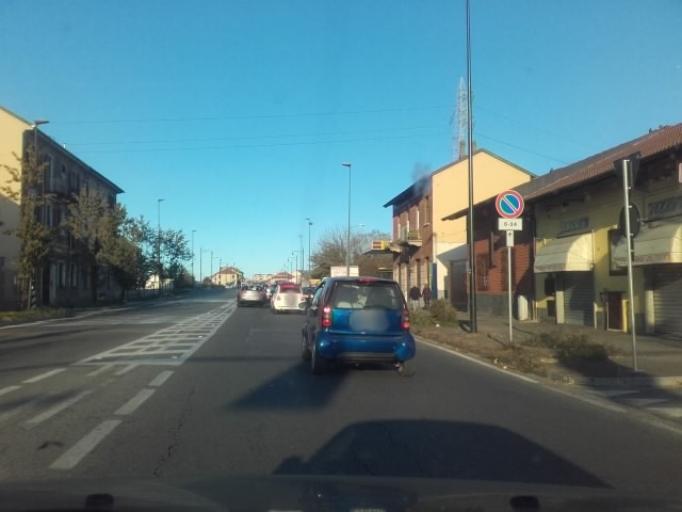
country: IT
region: Piedmont
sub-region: Provincia di Torino
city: Turin
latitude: 45.0970
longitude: 7.7199
